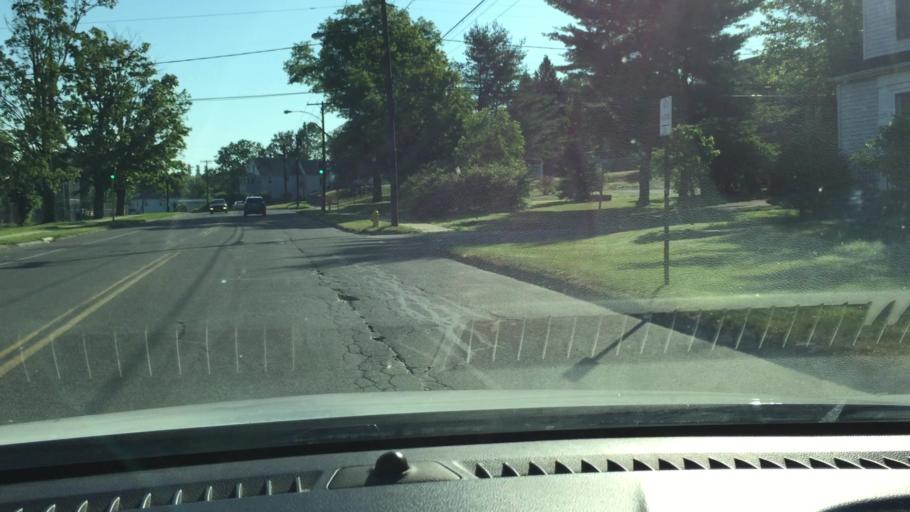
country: US
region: Massachusetts
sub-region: Berkshire County
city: Pittsfield
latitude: 42.4488
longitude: -73.2294
